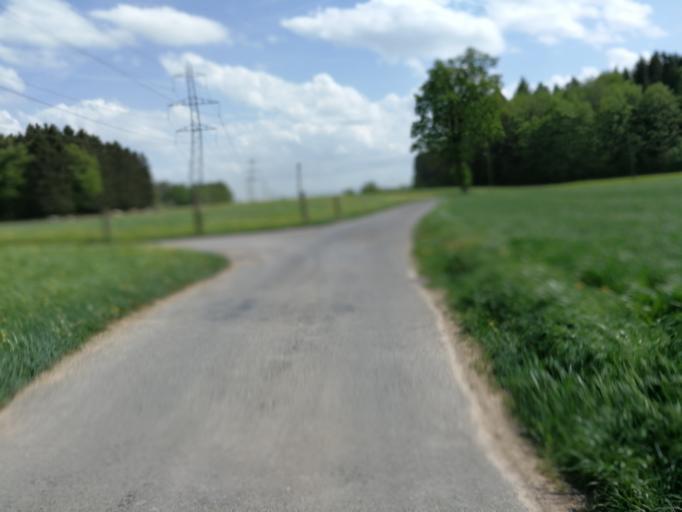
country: CH
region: Zurich
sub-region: Bezirk Meilen
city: Oetwil am See
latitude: 47.2839
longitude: 8.7371
